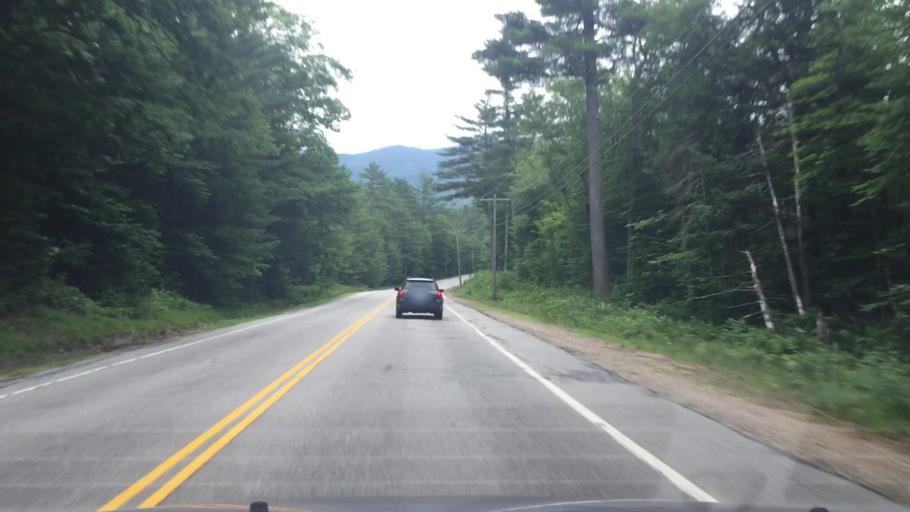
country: US
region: New Hampshire
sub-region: Carroll County
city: North Conway
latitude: 44.0754
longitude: -71.3079
